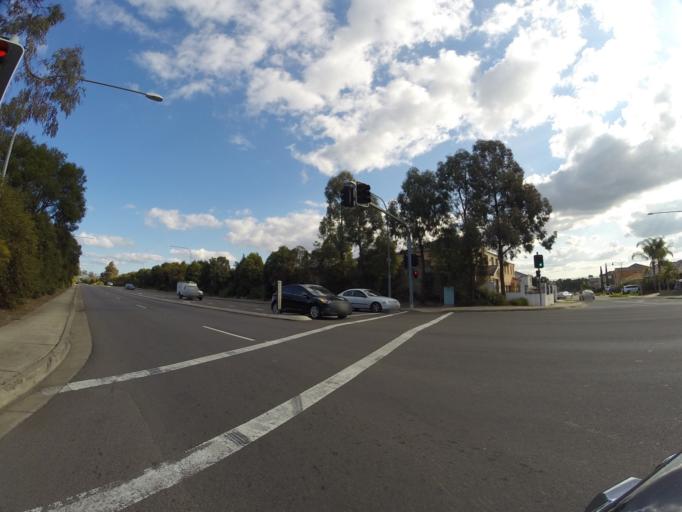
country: AU
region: New South Wales
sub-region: Campbelltown Municipality
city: Glenfield
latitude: -33.9533
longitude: 150.8828
